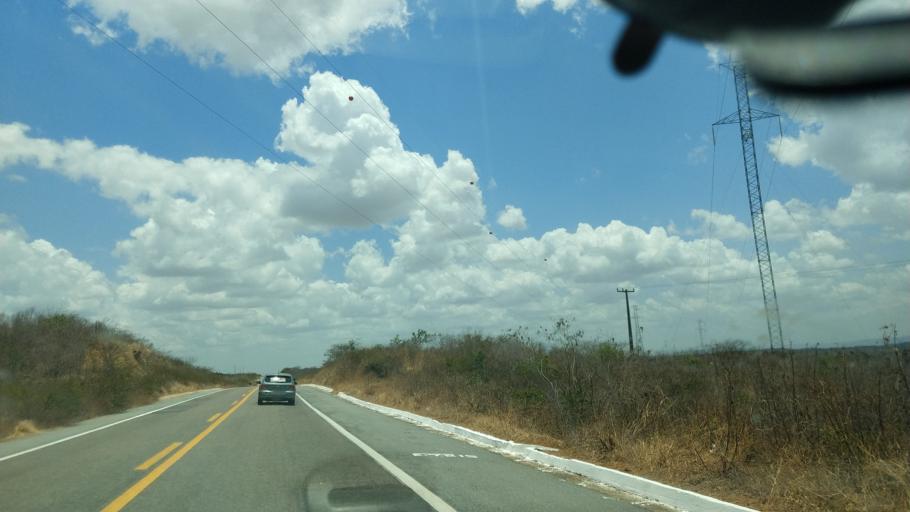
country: BR
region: Rio Grande do Norte
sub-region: Cerro Cora
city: Cerro Cora
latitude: -6.1942
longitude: -36.2620
